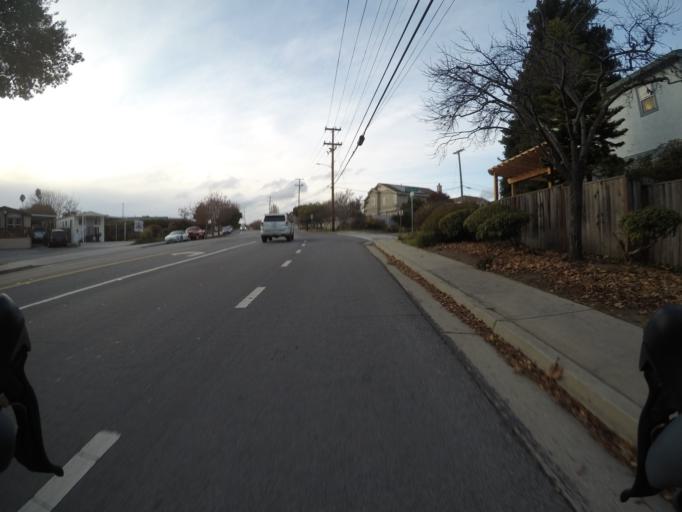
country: US
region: California
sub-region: Santa Cruz County
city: Live Oak
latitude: 36.9751
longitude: -121.9760
